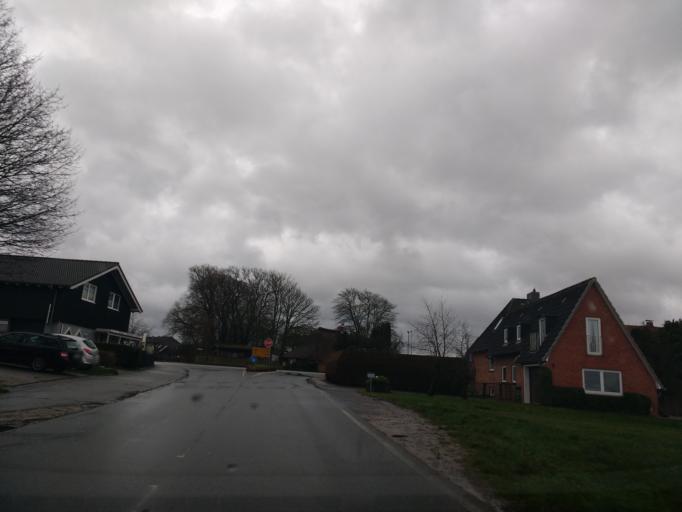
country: DE
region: Schleswig-Holstein
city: Blekendorf
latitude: 54.2826
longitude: 10.6788
